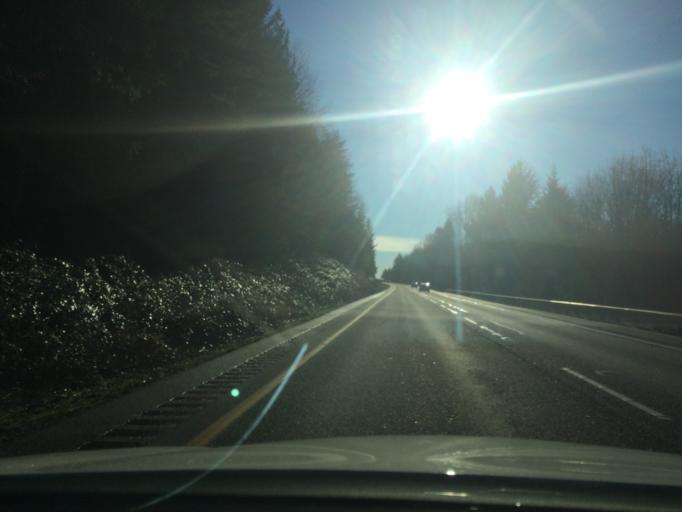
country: US
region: Washington
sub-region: Whatcom County
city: Sudden Valley
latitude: 48.6627
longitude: -122.3720
